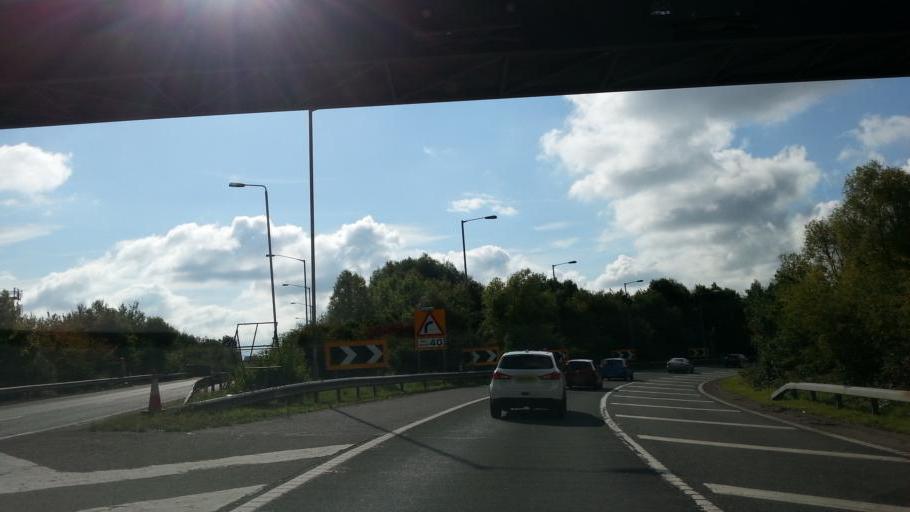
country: GB
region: England
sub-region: Buckinghamshire
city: Iver
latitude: 51.4980
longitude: -0.4935
